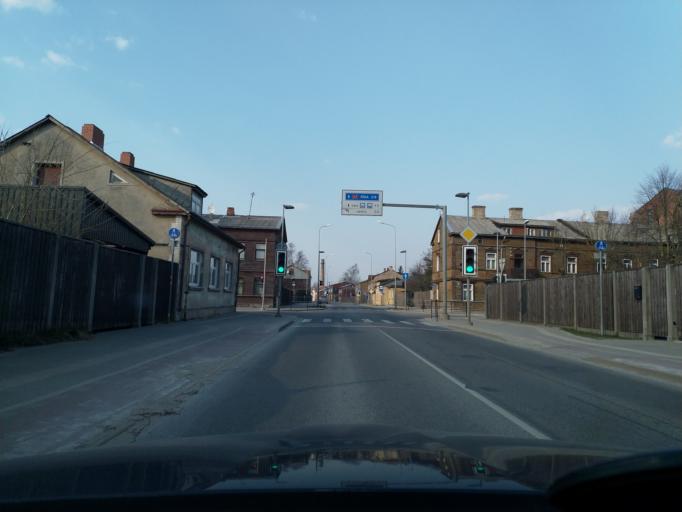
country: LV
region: Liepaja
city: Liepaja
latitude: 56.5053
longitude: 21.0244
